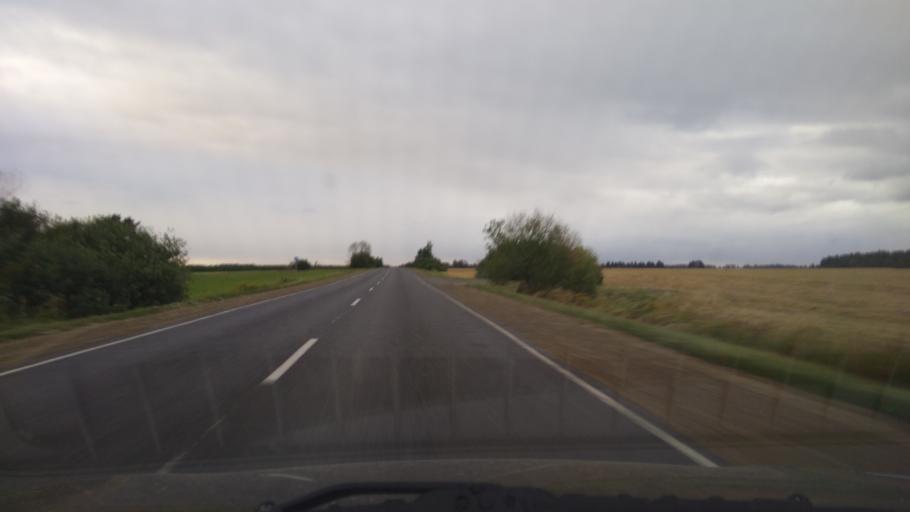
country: BY
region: Brest
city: Byaroza
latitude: 52.4387
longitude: 24.9777
